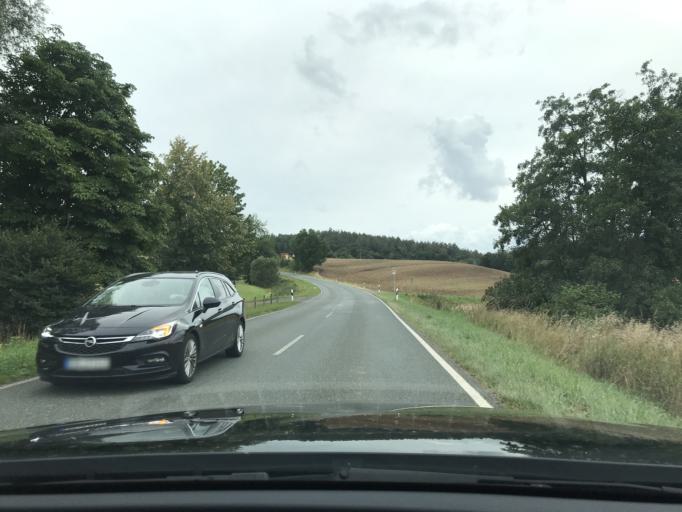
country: DE
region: Bavaria
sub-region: Regierungsbezirk Unterfranken
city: Burgpreppach
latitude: 50.1007
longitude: 10.6697
